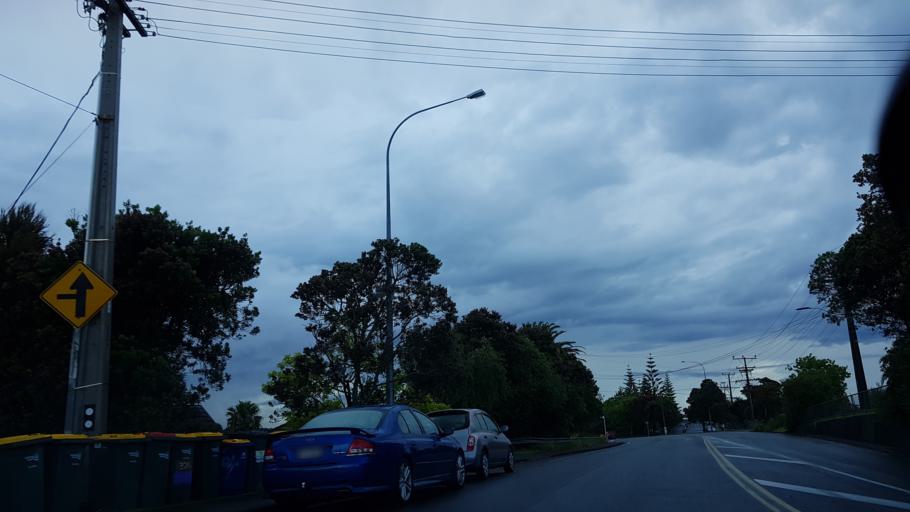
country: NZ
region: Auckland
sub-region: Auckland
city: North Shore
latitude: -36.7892
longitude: 174.7207
